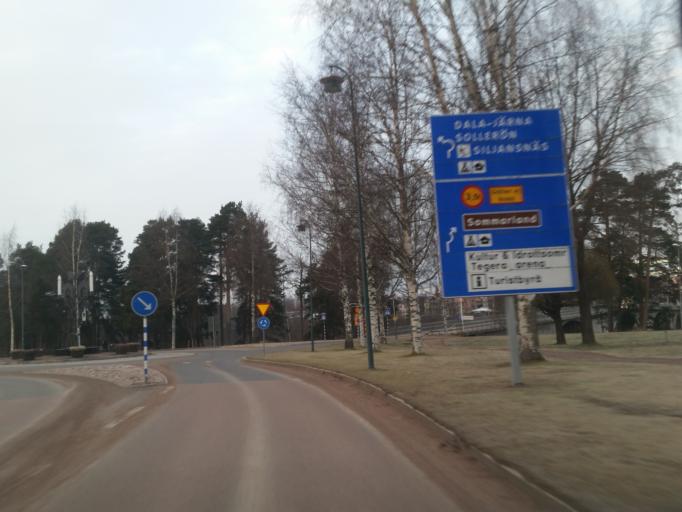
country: SE
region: Dalarna
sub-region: Leksand Municipality
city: Leksand
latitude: 60.7270
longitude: 14.9993
